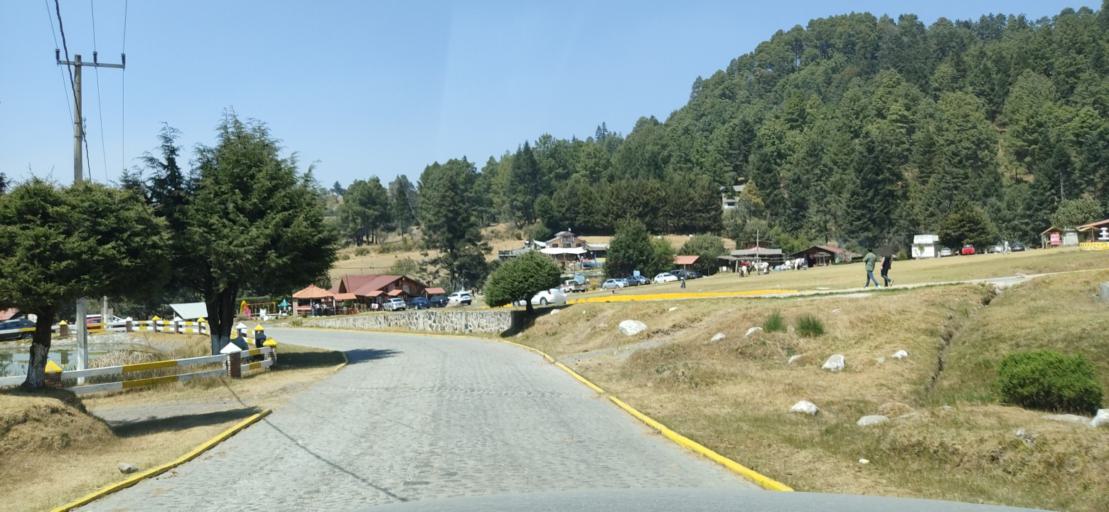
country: MX
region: Mexico
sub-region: Ocoyoacac
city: San Jeronimo Acazulco
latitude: 19.2418
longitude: -99.3797
